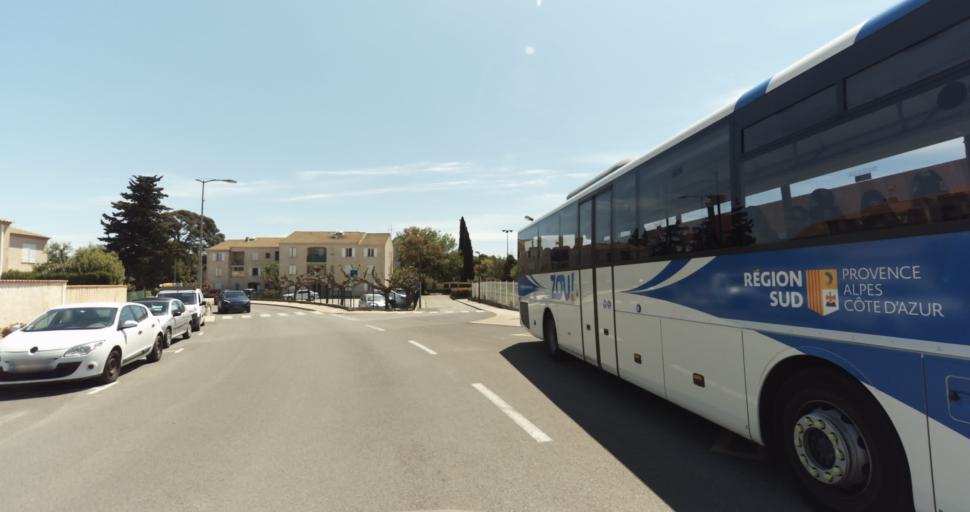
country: FR
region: Provence-Alpes-Cote d'Azur
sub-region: Departement du Var
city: La Crau
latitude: 43.1459
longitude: 6.0697
